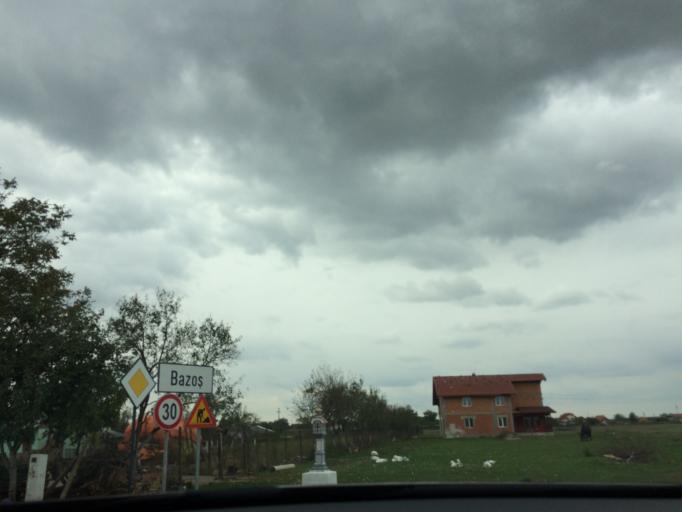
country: RO
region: Timis
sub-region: Oras Recas
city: Recas
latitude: 45.7430
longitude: 21.4982
